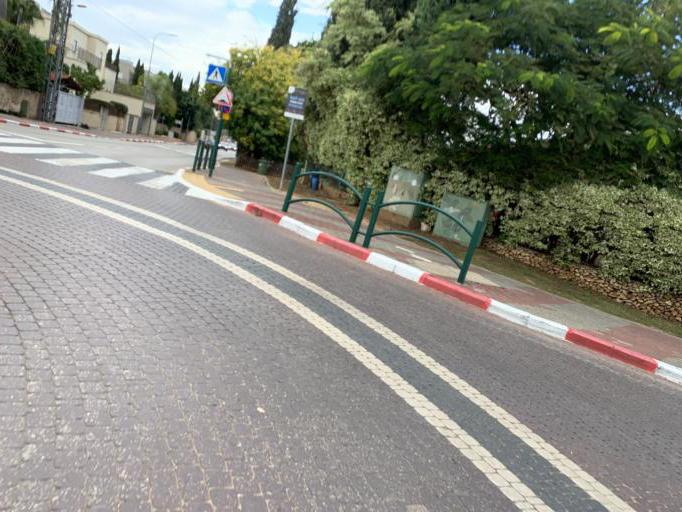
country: IL
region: Central District
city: Hod HaSharon
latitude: 32.1587
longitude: 34.8871
